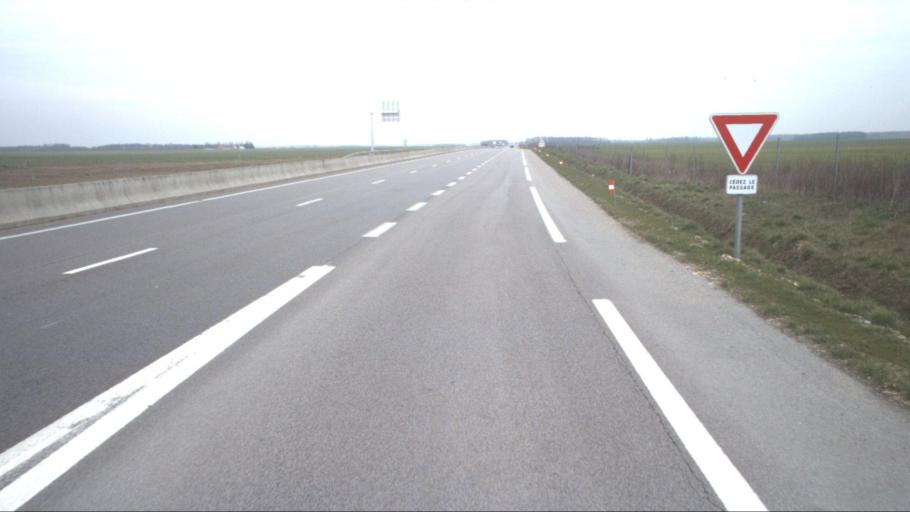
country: FR
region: Ile-de-France
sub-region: Departement des Yvelines
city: Sonchamp
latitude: 48.5818
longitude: 1.8324
